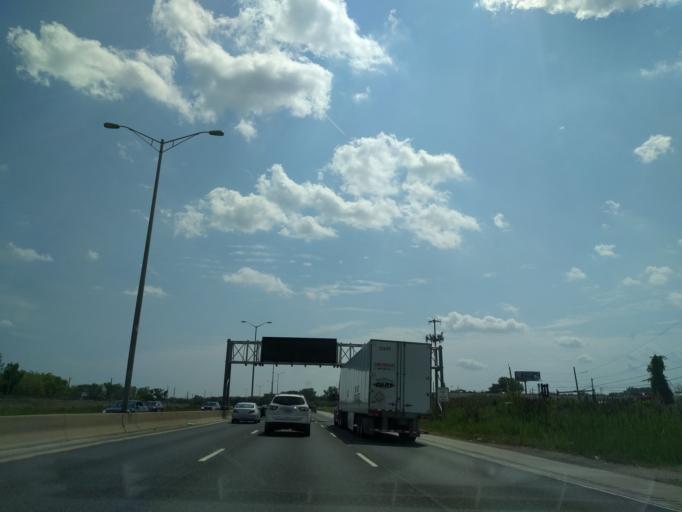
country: US
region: Illinois
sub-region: Cook County
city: Dolton
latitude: 41.6786
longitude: -87.6017
